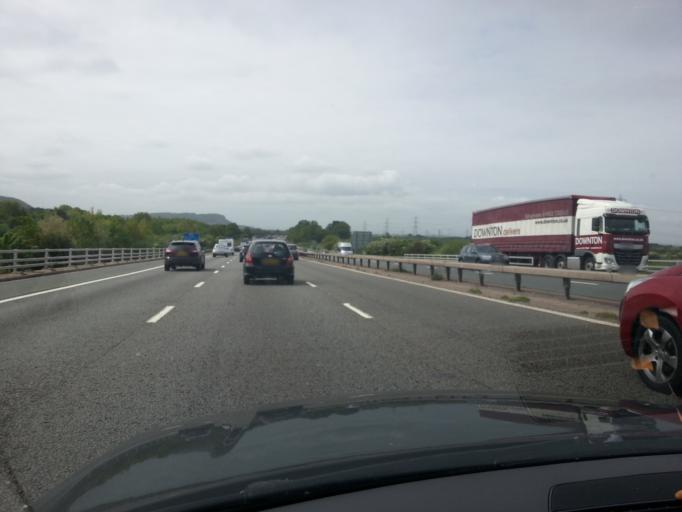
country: GB
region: England
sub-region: Cheshire West and Chester
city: Frodsham
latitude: 53.3060
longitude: -2.7152
